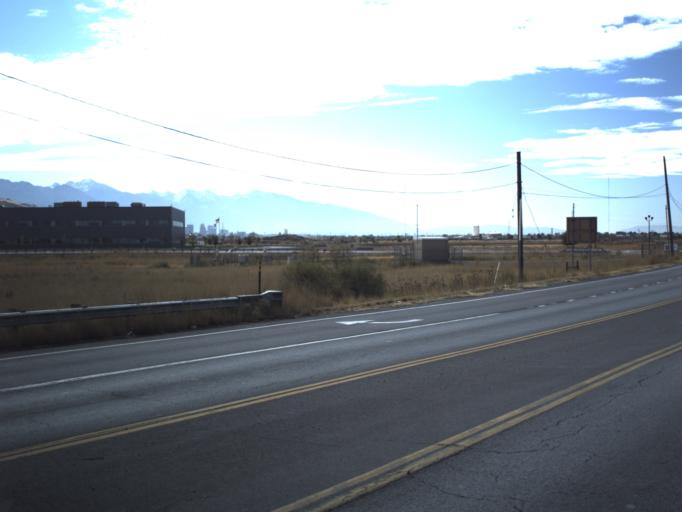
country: US
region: Utah
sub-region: Davis County
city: North Salt Lake
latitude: 40.8319
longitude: -111.9368
